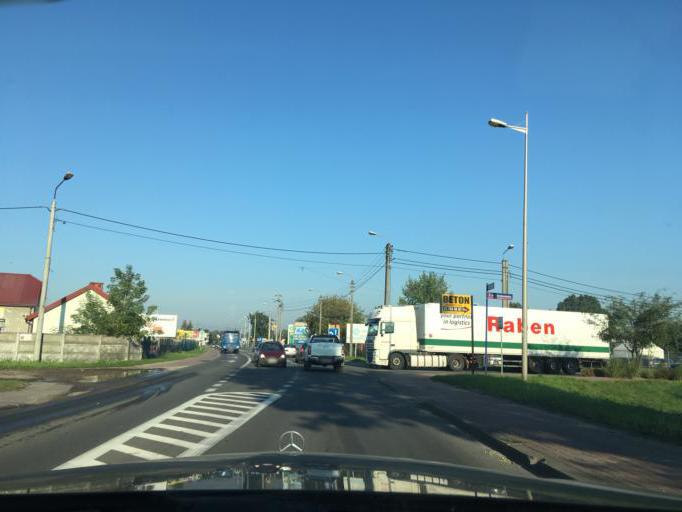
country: PL
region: Masovian Voivodeship
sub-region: Powiat grodziski
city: Grodzisk Mazowiecki
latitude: 52.1144
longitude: 20.6258
